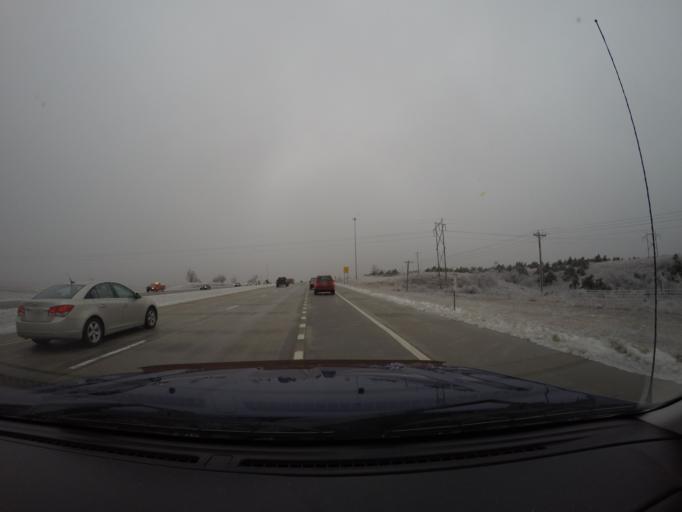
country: US
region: Kansas
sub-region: Riley County
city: Manhattan
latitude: 39.0629
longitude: -96.5337
